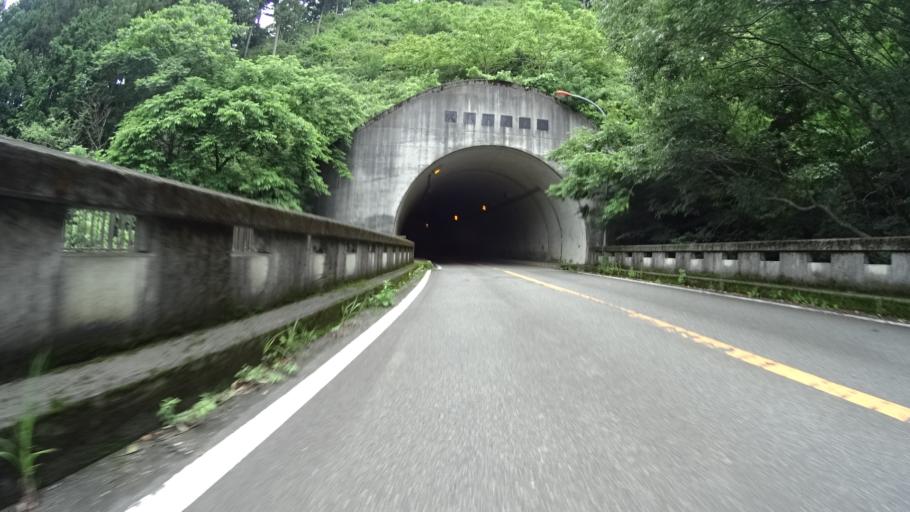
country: JP
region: Kanagawa
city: Hadano
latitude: 35.5132
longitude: 139.2318
